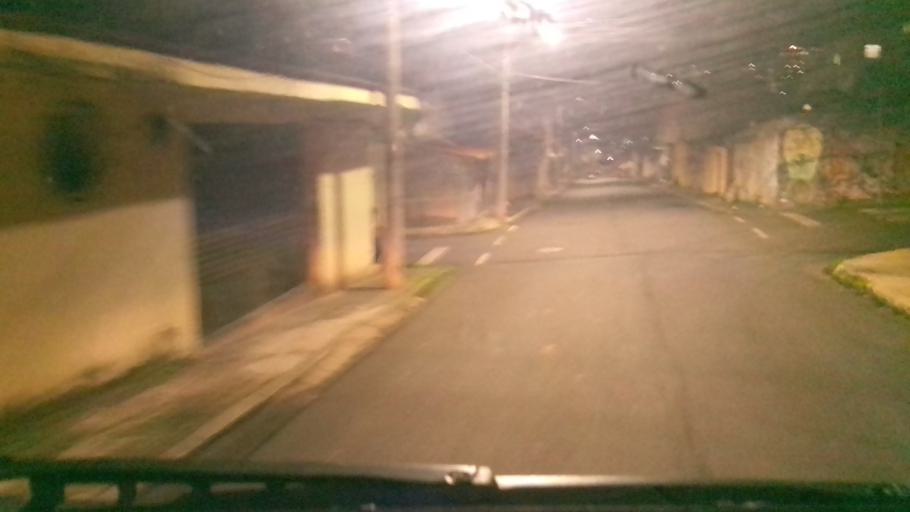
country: BR
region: Minas Gerais
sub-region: Belo Horizonte
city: Belo Horizonte
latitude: -19.9104
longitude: -43.9027
